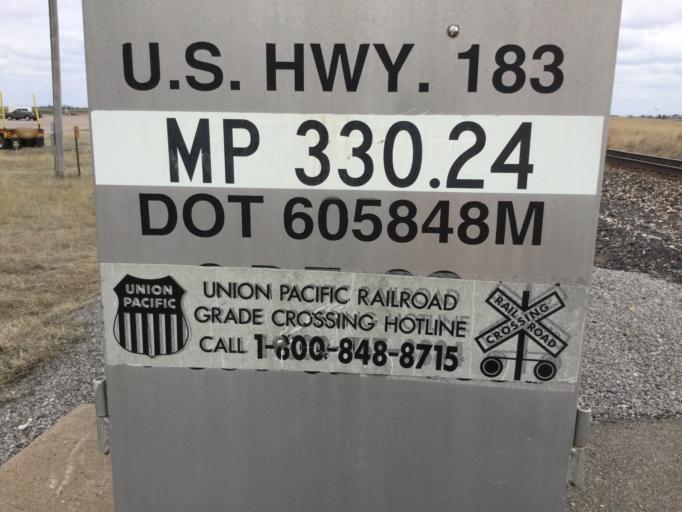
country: US
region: Kansas
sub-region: Kiowa County
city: Greensburg
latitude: 37.6073
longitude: -99.3219
